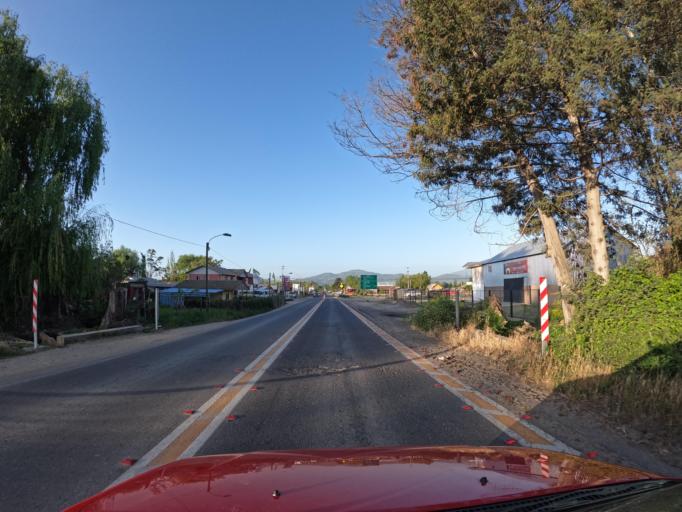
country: CL
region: O'Higgins
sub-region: Provincia de Cachapoal
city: San Vicente
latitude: -34.3126
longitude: -71.3846
